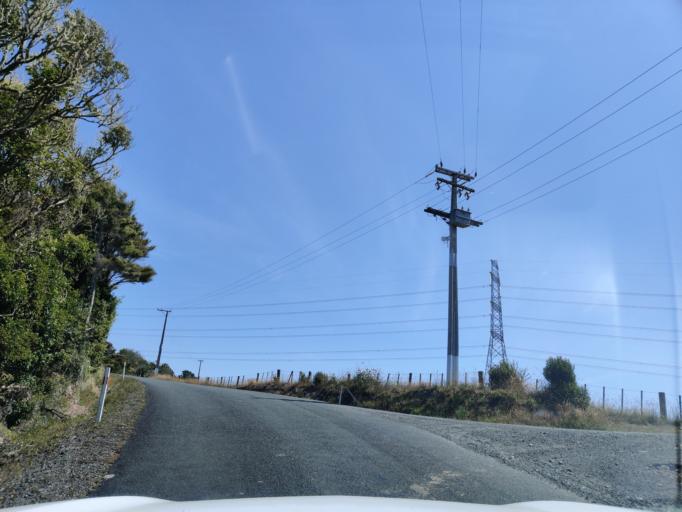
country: NZ
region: Auckland
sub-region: Auckland
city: Red Hill
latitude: -37.0663
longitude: 175.0750
